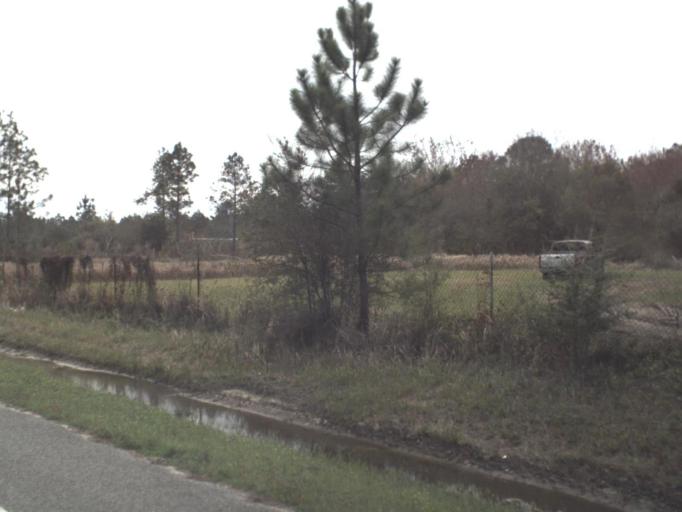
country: US
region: Florida
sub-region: Gulf County
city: Wewahitchka
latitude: 30.0334
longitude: -85.1824
